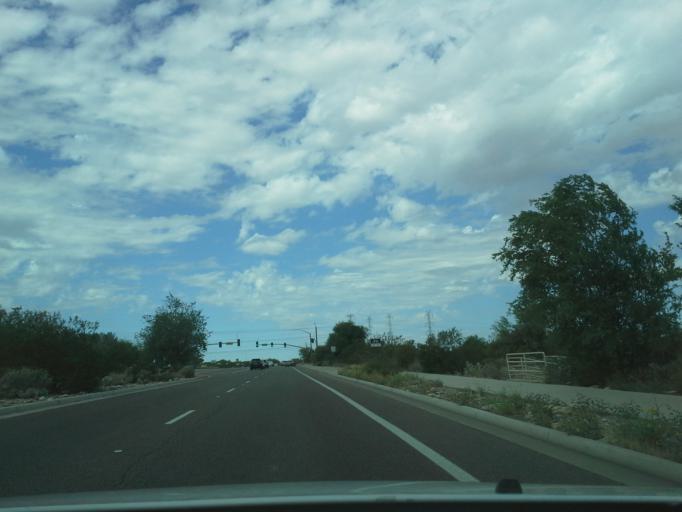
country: US
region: Arizona
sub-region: Maricopa County
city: Paradise Valley
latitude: 33.6402
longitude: -111.8764
